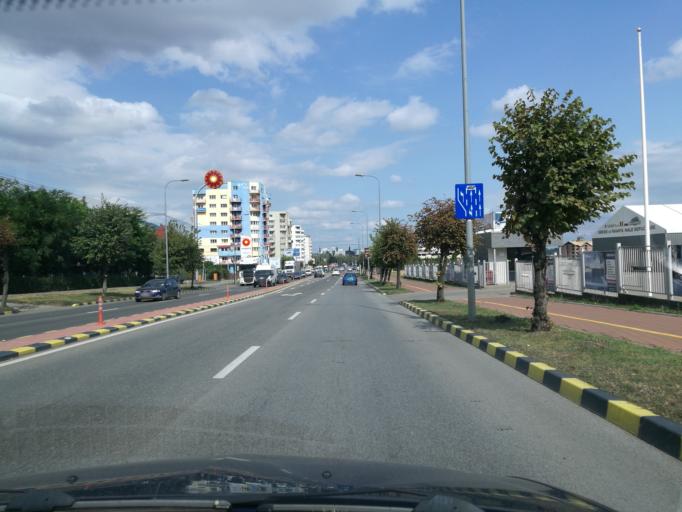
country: RO
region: Suceava
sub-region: Comuna Scheia
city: Scheia
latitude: 47.6346
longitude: 26.2325
